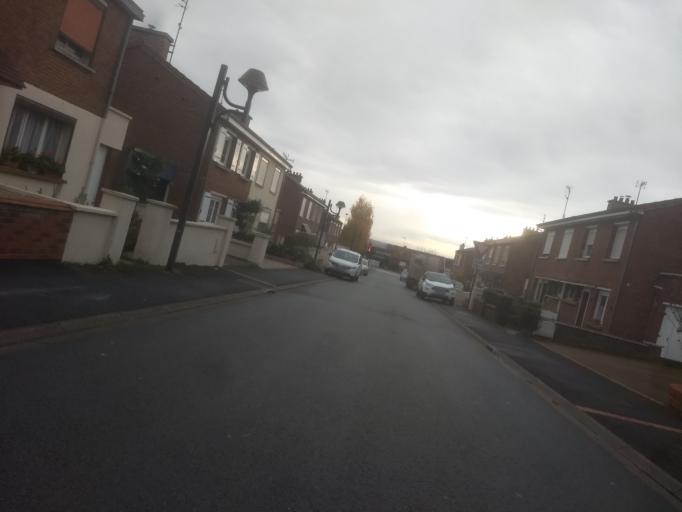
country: FR
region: Nord-Pas-de-Calais
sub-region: Departement du Pas-de-Calais
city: Dainville
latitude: 50.2869
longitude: 2.7415
